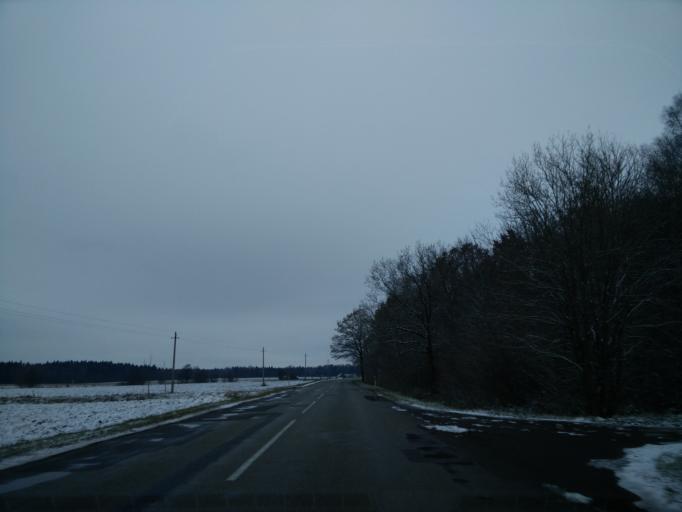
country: LT
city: Ariogala
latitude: 55.3984
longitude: 23.3393
